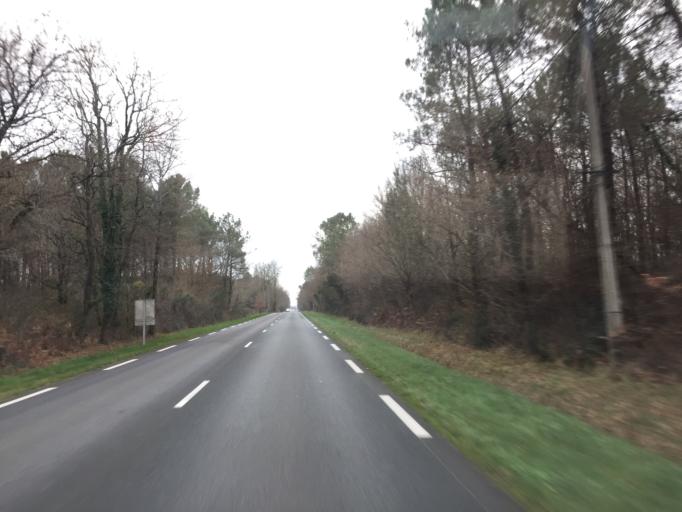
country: FR
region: Aquitaine
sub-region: Departement de la Gironde
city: Saint-Sauveur
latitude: 45.1874
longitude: -0.8488
